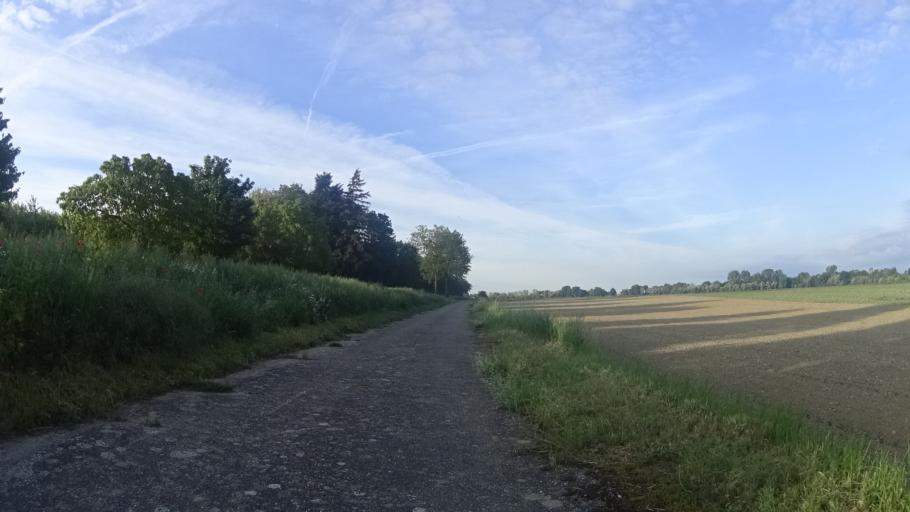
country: DE
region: Baden-Wuerttemberg
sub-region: Freiburg Region
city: Hartheim
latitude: 47.9771
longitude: 7.6444
